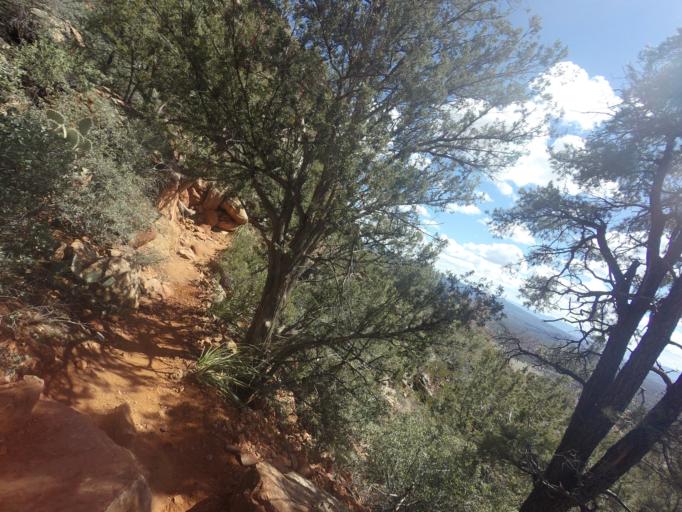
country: US
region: Arizona
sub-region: Yavapai County
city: West Sedona
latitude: 34.9029
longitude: -111.8727
